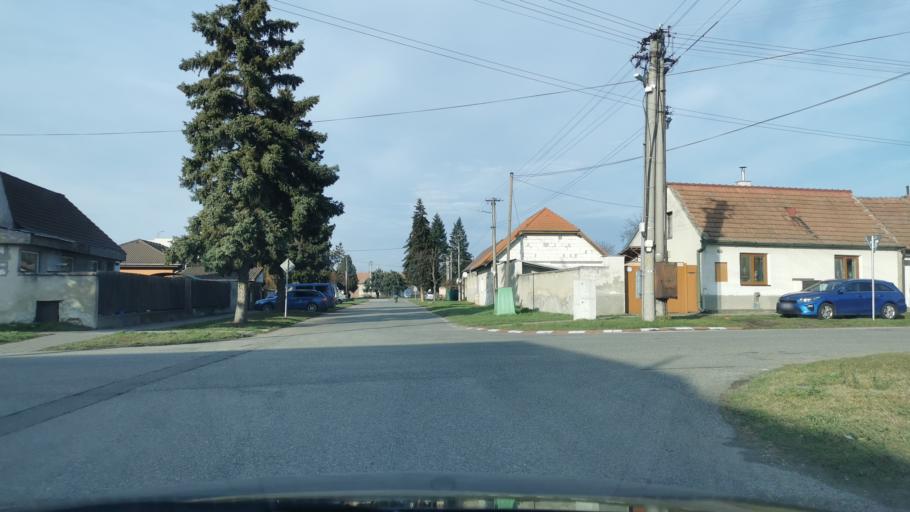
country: SK
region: Trnavsky
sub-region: Okres Skalica
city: Holic
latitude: 48.7851
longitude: 17.1107
